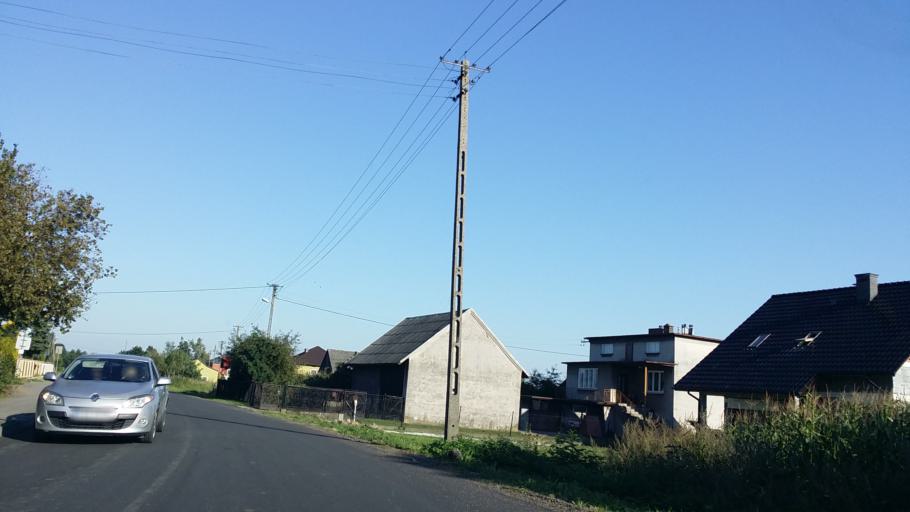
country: PL
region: Lesser Poland Voivodeship
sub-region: Powiat wadowicki
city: Spytkowice
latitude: 50.0157
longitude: 19.5082
